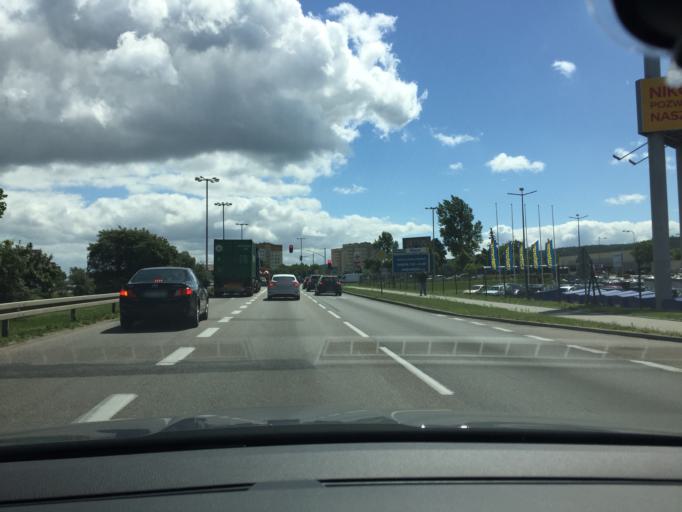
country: PL
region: Pomeranian Voivodeship
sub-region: Powiat wejherowski
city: Rumia
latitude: 54.5715
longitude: 18.3861
